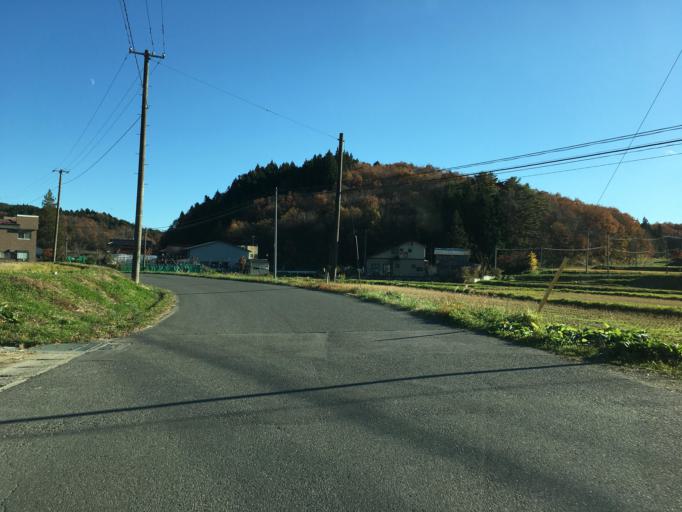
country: JP
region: Fukushima
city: Ishikawa
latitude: 37.2335
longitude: 140.5488
